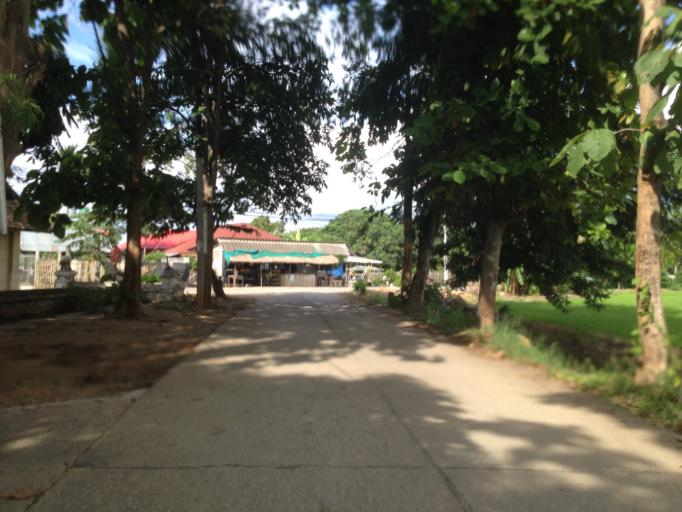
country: TH
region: Chiang Mai
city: Hang Dong
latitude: 18.7213
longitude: 98.9335
